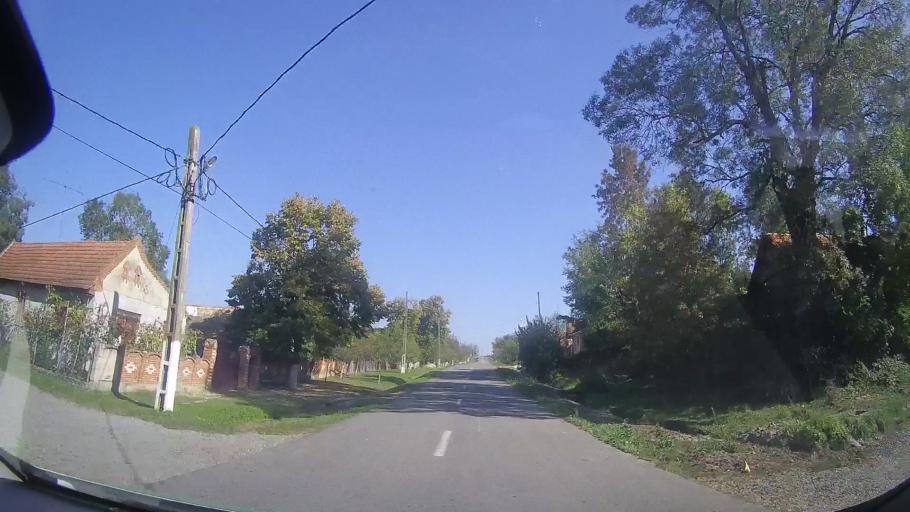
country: RO
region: Timis
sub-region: Comuna Balint
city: Balint
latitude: 45.8443
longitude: 21.8616
